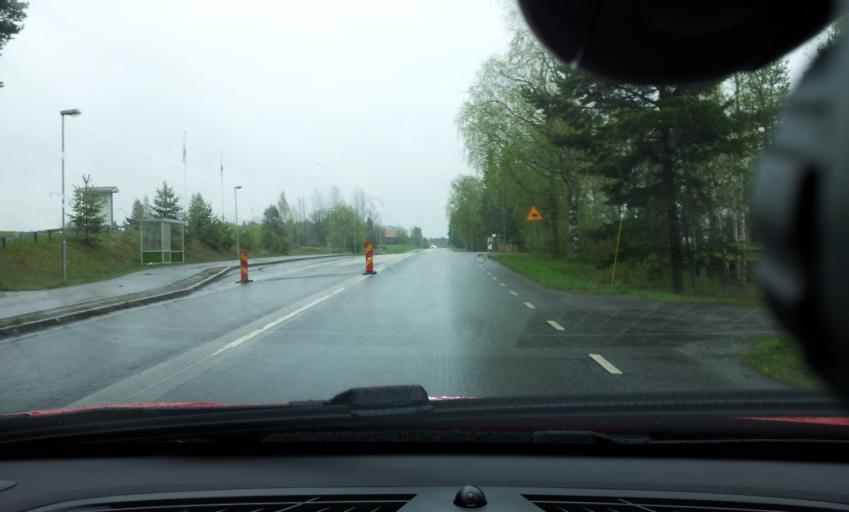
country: SE
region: Jaemtland
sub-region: OEstersunds Kommun
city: Ostersund
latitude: 63.1434
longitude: 14.7291
